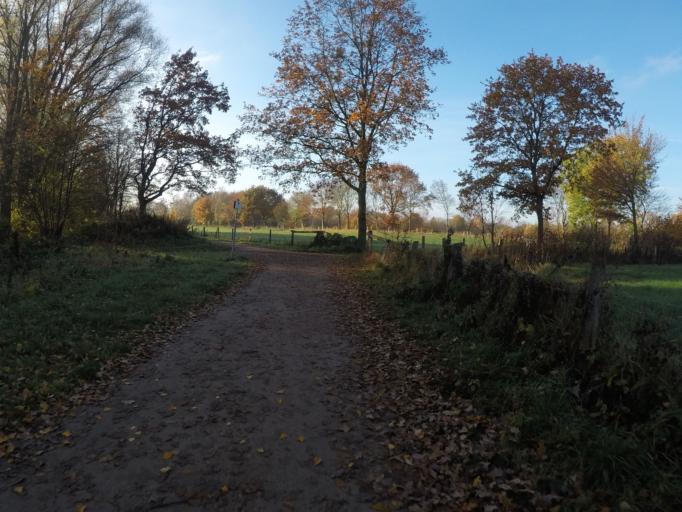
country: DE
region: Hamburg
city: Eidelstedt
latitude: 53.6122
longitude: 9.9219
